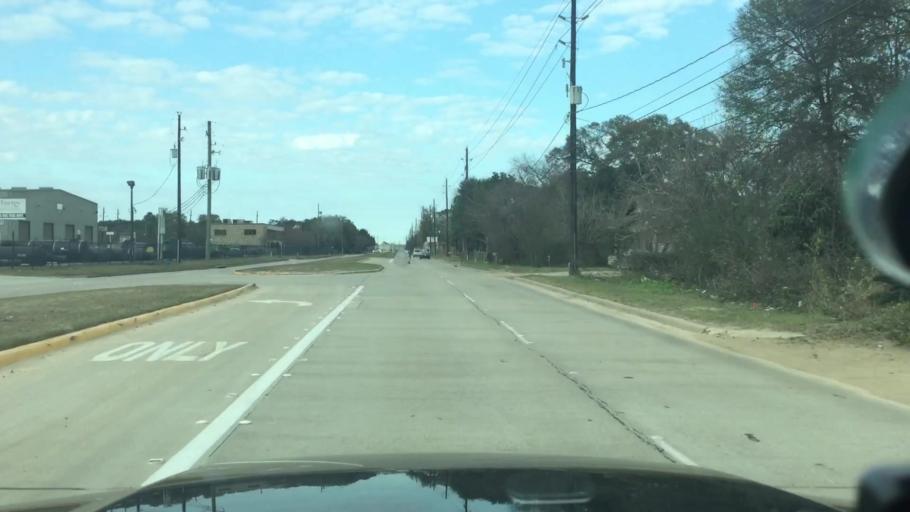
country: US
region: Texas
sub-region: Harris County
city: Hudson
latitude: 29.9170
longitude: -95.5250
